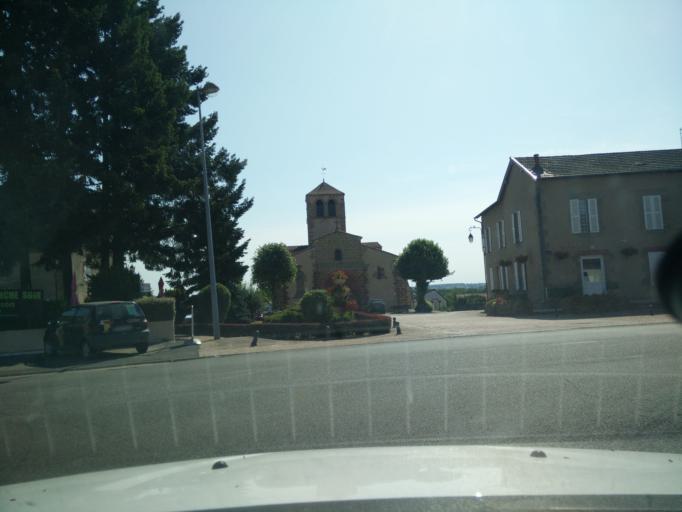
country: FR
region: Auvergne
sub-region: Departement de l'Allier
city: Toulon-sur-Allier
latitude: 46.4889
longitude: 3.3151
